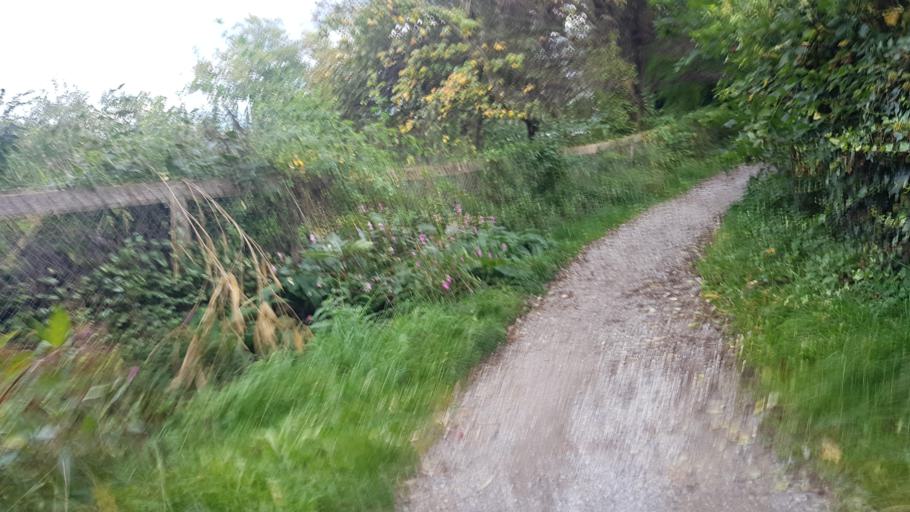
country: DE
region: Baden-Wuerttemberg
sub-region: Tuebingen Region
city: Friedrichshafen
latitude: 47.6577
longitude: 9.4402
